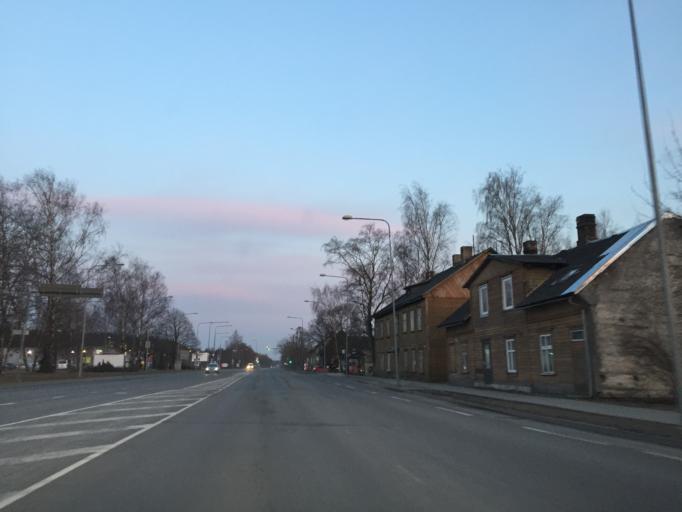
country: EE
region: Paernumaa
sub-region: Paernu linn
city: Parnu
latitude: 58.3699
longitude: 24.5478
